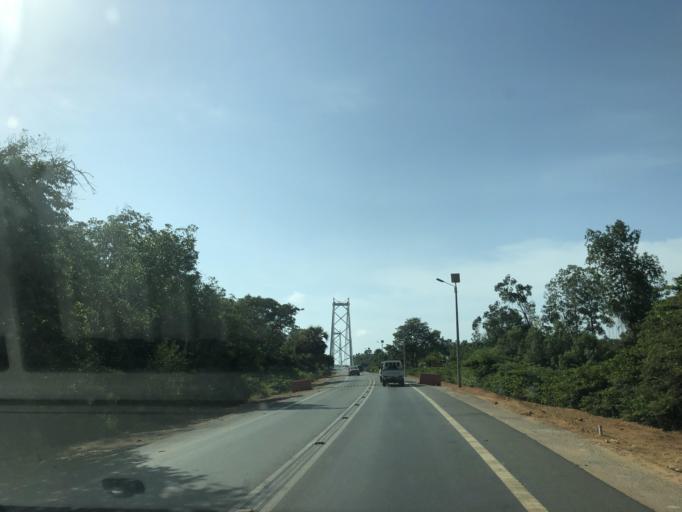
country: AO
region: Luanda
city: Luanda
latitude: -9.3263
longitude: 13.1673
